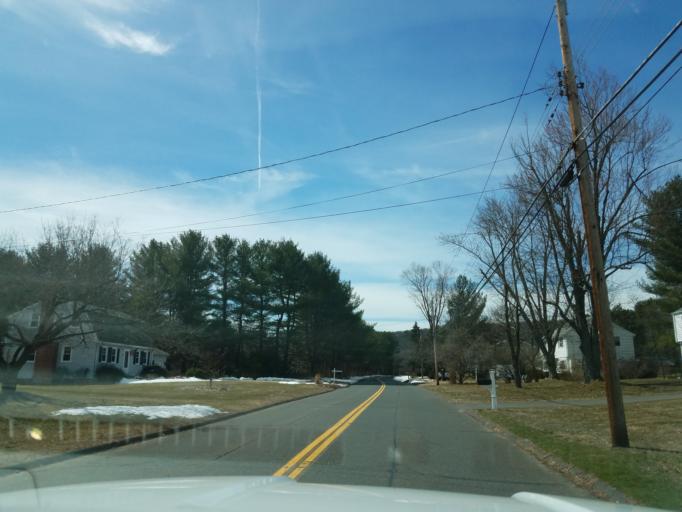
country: US
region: Connecticut
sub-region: Hartford County
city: Canton Valley
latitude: 41.8037
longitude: -72.8853
